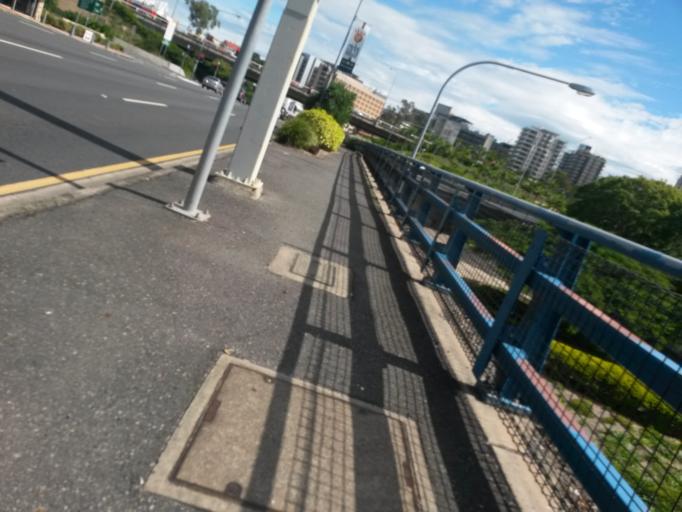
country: AU
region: Queensland
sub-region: Brisbane
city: Woolloongabba
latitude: -27.4861
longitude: 153.0334
